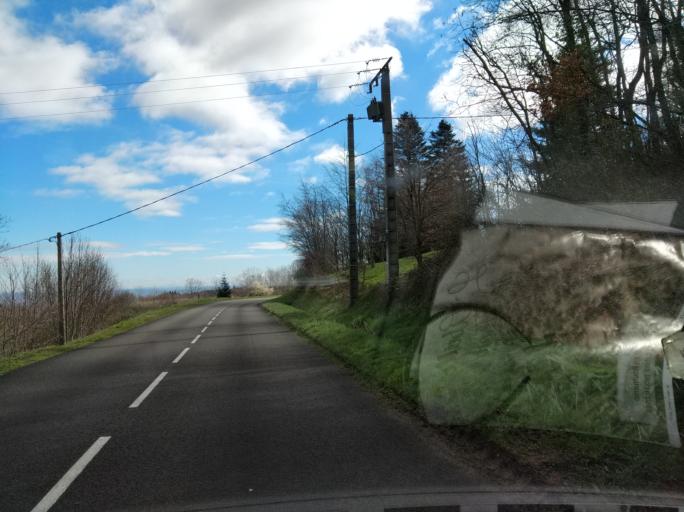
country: FR
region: Rhone-Alpes
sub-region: Departement de la Loire
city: Pelussin
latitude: 45.4120
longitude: 4.6730
